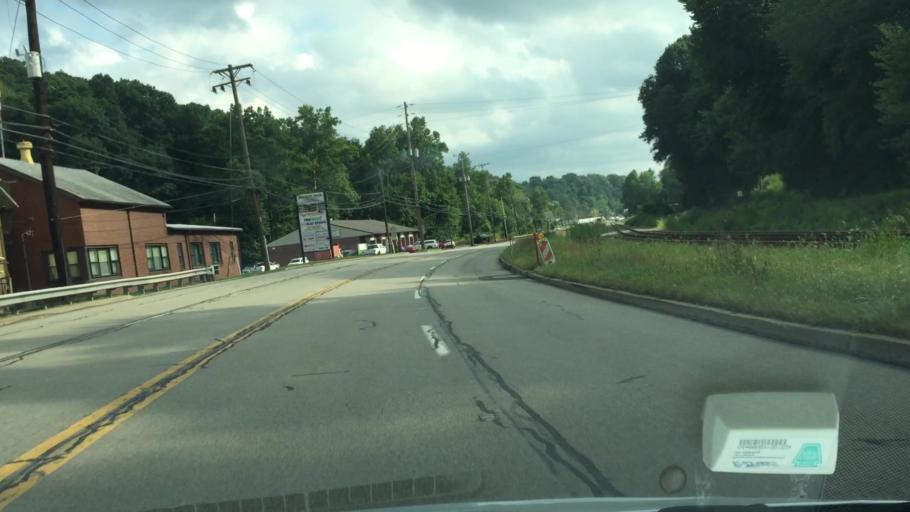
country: US
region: Pennsylvania
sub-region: Allegheny County
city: Allison Park
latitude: 40.5553
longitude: -79.9582
